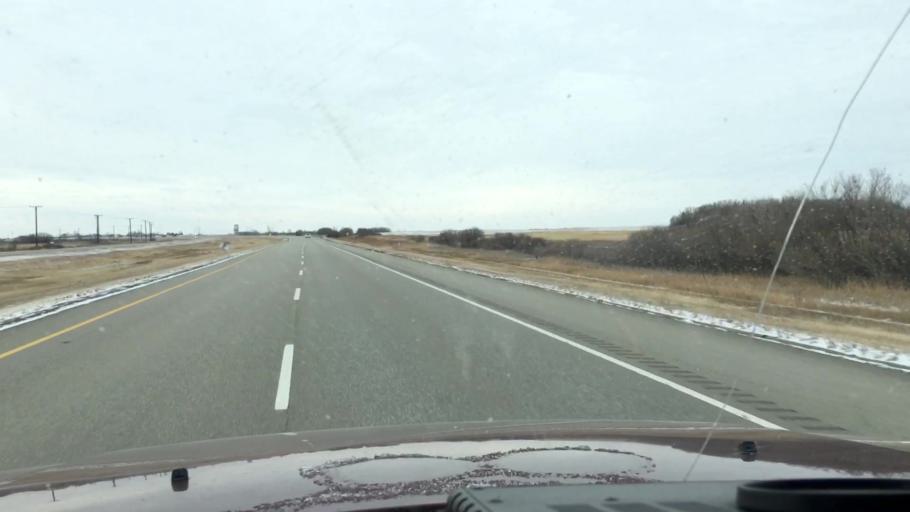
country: CA
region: Saskatchewan
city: Watrous
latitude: 51.3845
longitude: -106.1626
